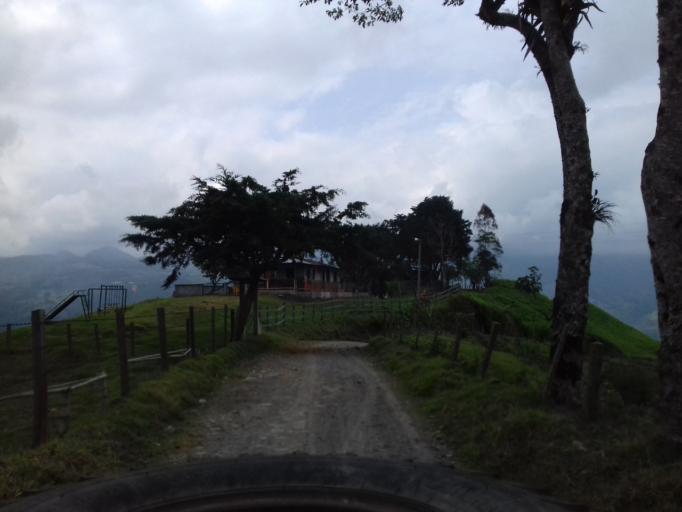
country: CO
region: Tolima
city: Libano
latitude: 4.9389
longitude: -75.0627
